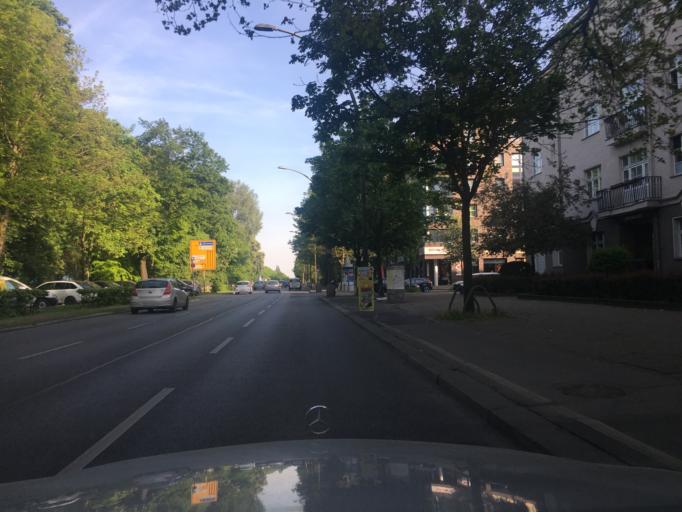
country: DE
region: Berlin
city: Plaenterwald
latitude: 52.4831
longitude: 13.4702
